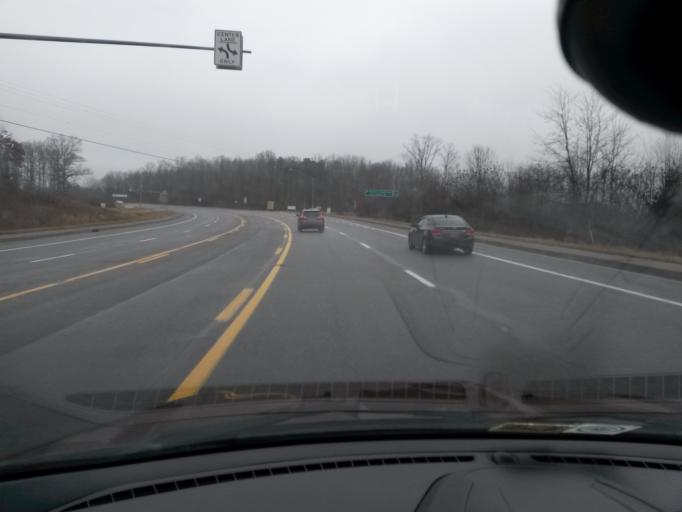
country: US
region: West Virginia
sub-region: Raleigh County
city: Stanaford
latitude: 37.7815
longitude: -81.1524
